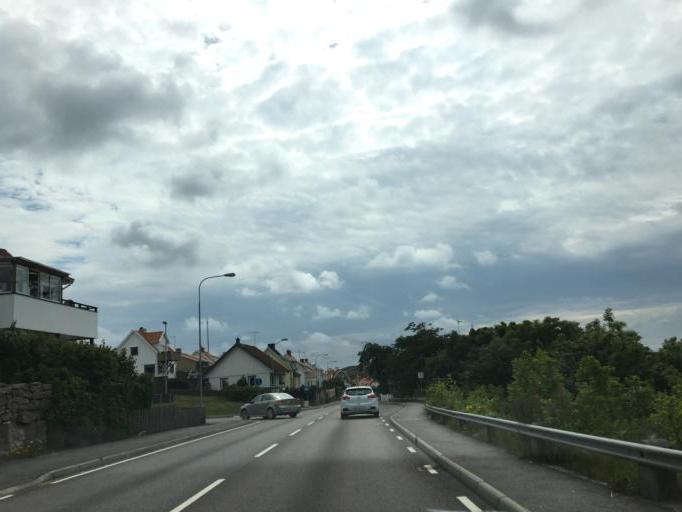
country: SE
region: Vaestra Goetaland
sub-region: Sotenas Kommun
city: Kungshamn
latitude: 58.3666
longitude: 11.2496
